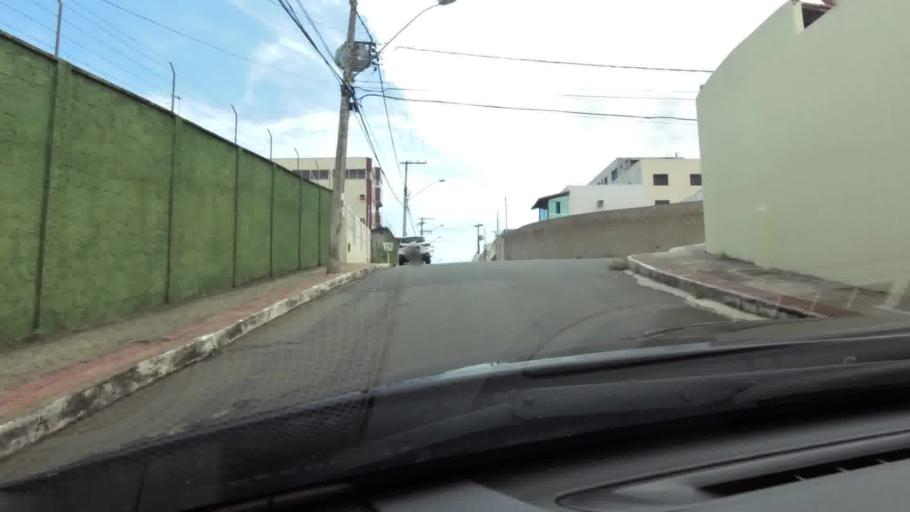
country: BR
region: Espirito Santo
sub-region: Guarapari
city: Guarapari
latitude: -20.6533
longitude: -40.5022
